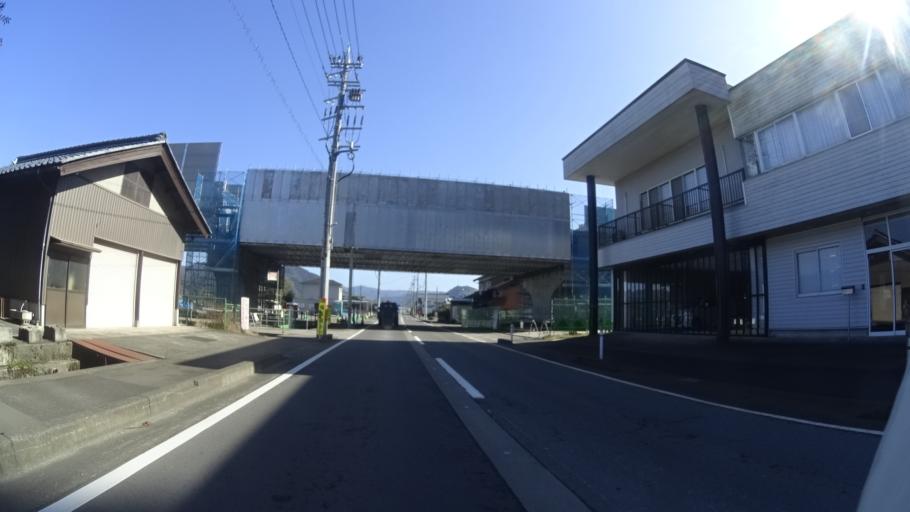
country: JP
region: Fukui
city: Sabae
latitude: 35.9484
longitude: 136.2174
